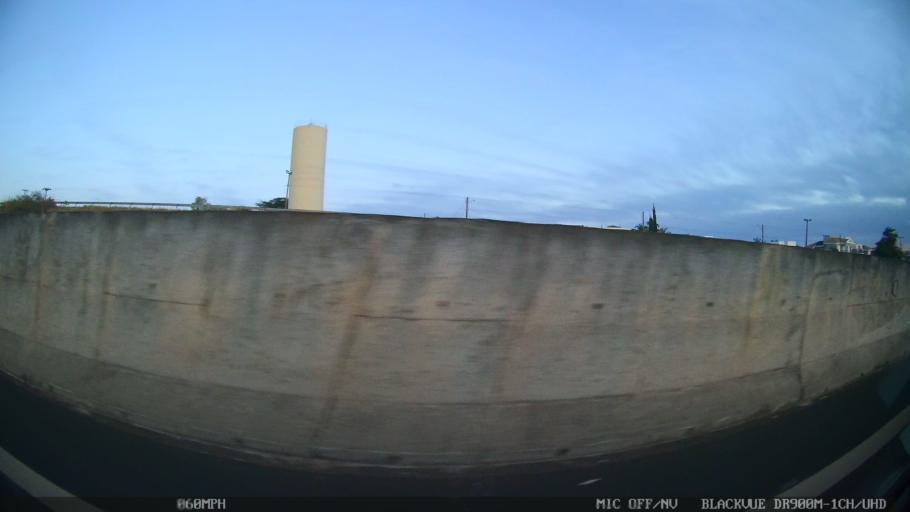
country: BR
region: Sao Paulo
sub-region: Catanduva
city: Catanduva
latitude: -21.1164
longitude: -48.9801
